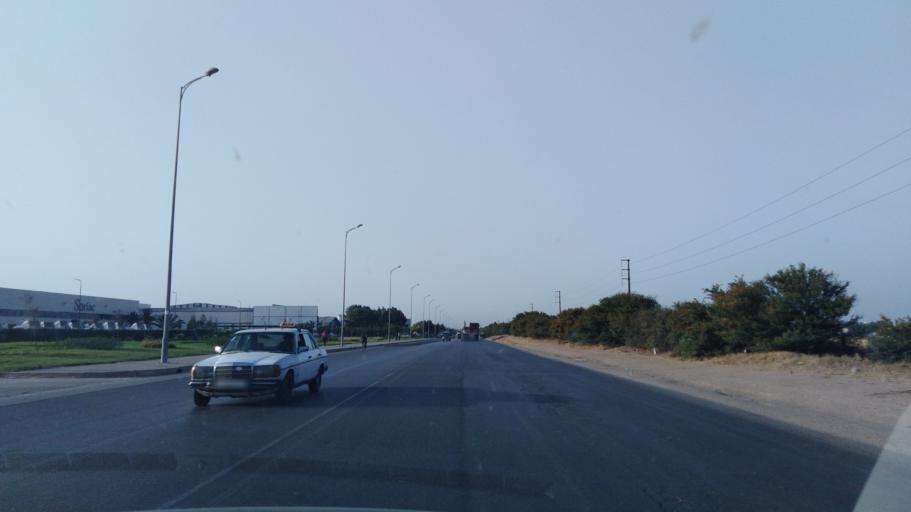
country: MA
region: Chaouia-Ouardigha
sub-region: Settat Province
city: Berrechid
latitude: 33.2479
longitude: -7.5855
